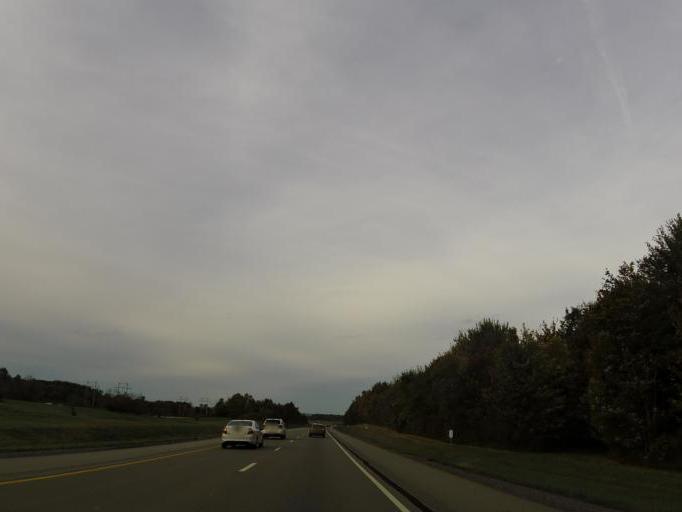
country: US
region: New York
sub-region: Erie County
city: Angola
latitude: 42.6188
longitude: -79.0096
